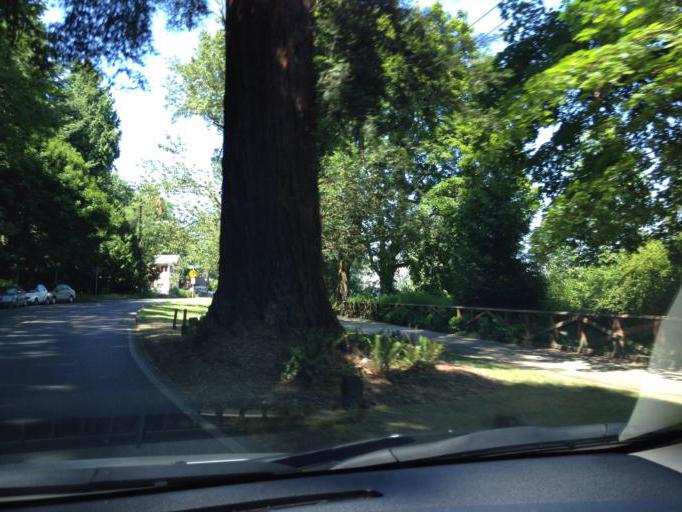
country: US
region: Washington
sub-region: King County
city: Seattle
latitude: 47.6107
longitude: -122.2829
